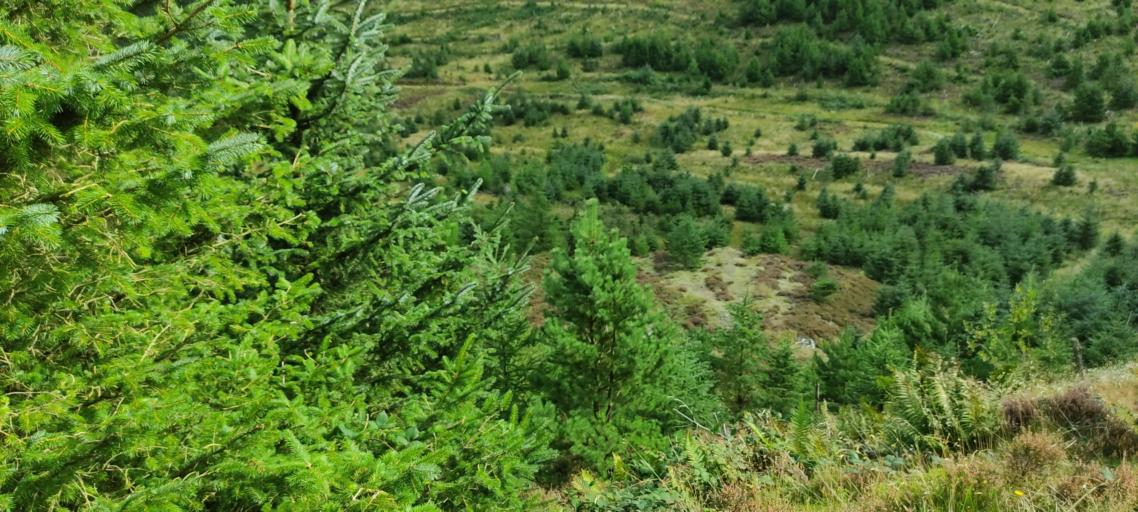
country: GB
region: England
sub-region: Cumbria
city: Frizington
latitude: 54.5596
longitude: -3.3956
